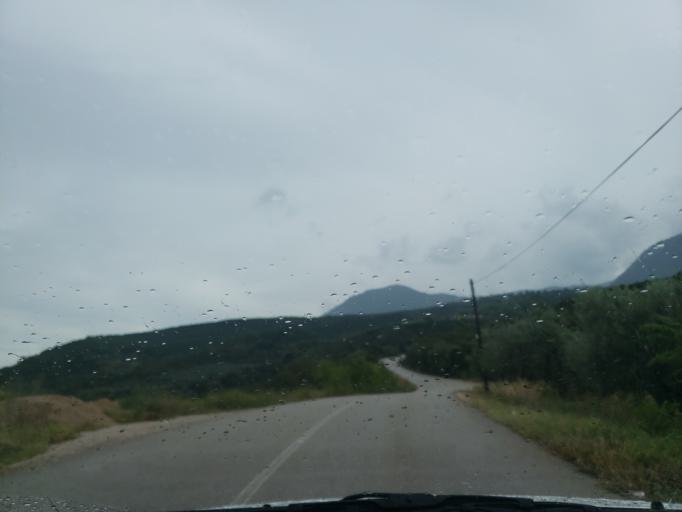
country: GR
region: Central Greece
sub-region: Nomos Fthiotidos
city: Anthili
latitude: 38.7977
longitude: 22.4799
